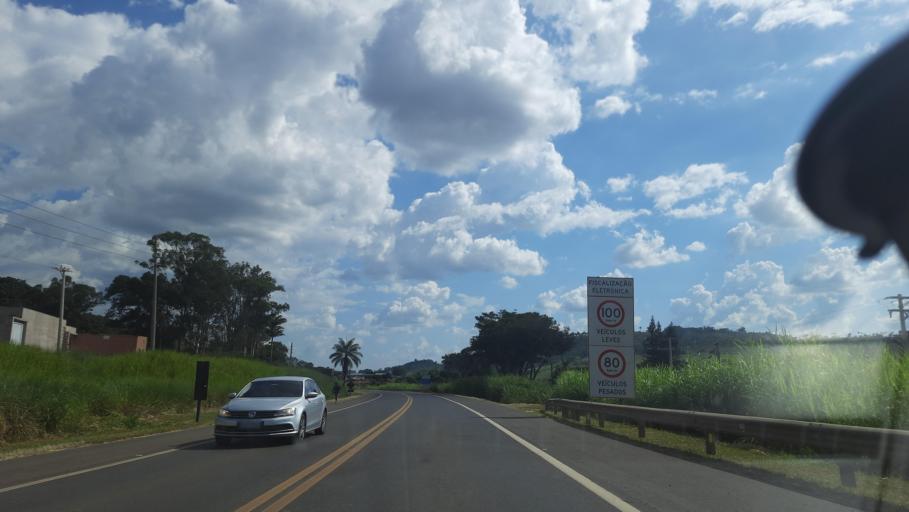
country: BR
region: Sao Paulo
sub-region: Sao Jose Do Rio Pardo
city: Sao Jose do Rio Pardo
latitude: -21.6313
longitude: -46.9015
